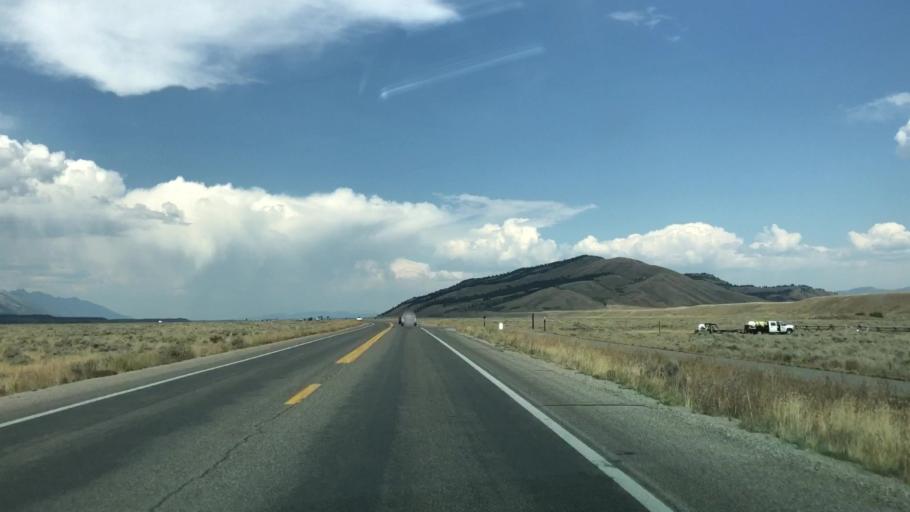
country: US
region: Wyoming
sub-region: Teton County
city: Jackson
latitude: 43.5951
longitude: -110.7258
